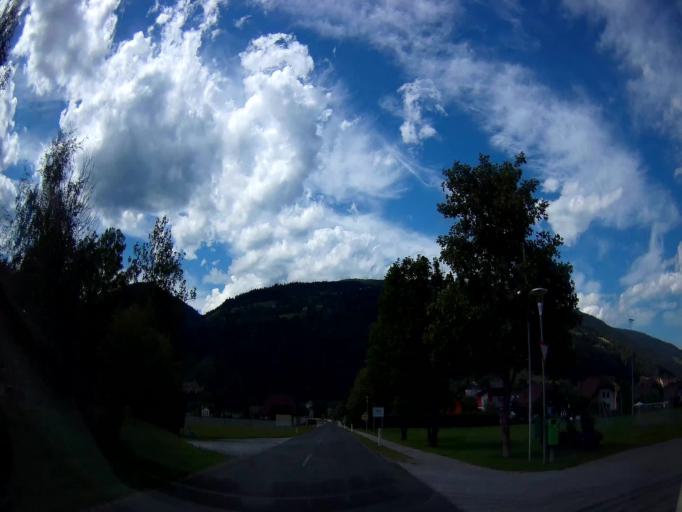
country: AT
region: Styria
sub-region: Politischer Bezirk Murau
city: Stadl an der Mur
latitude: 47.0816
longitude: 13.9812
